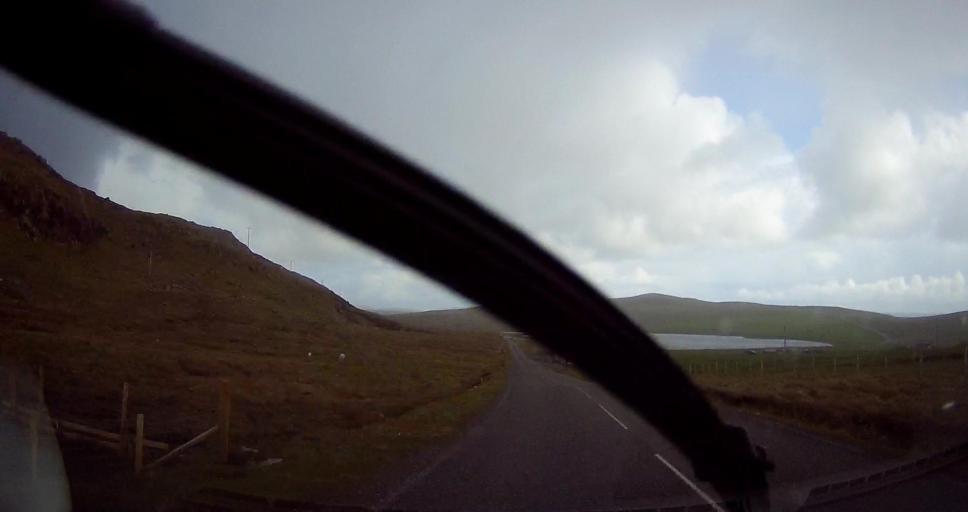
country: GB
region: Scotland
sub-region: Shetland Islands
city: Lerwick
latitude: 60.5445
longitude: -1.3425
